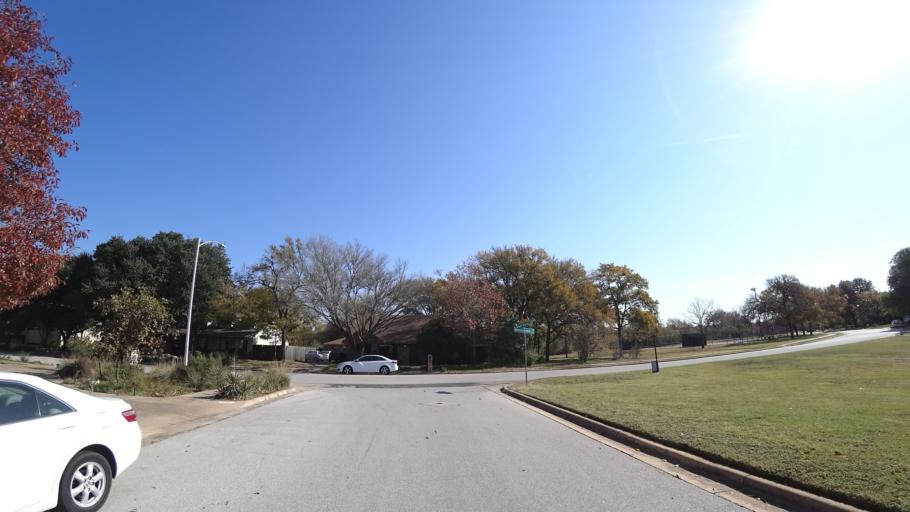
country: US
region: Texas
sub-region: Travis County
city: Shady Hollow
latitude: 30.2225
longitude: -97.8539
